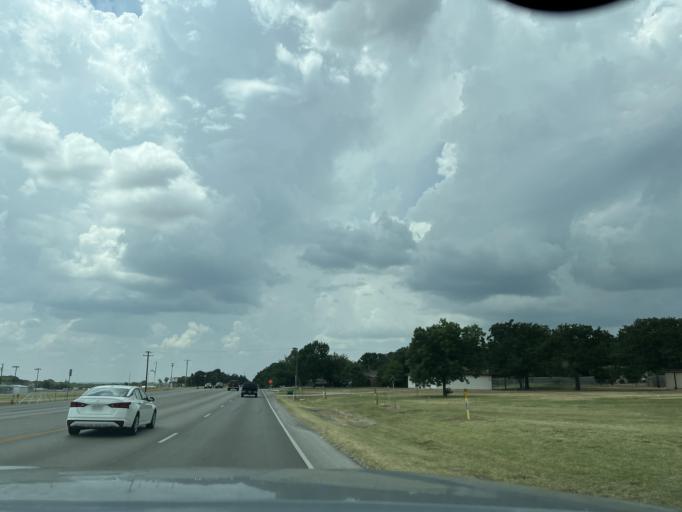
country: US
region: Texas
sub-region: Wise County
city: Decatur
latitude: 33.2076
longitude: -97.6011
